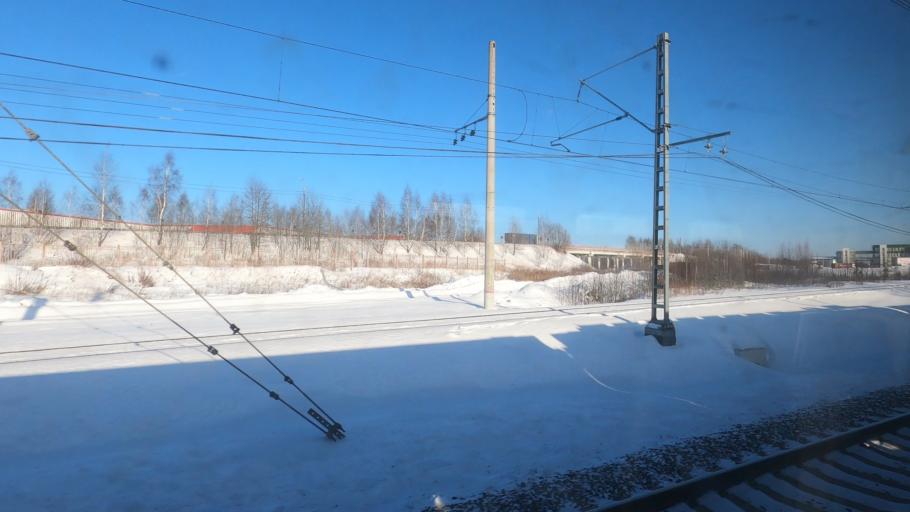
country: RU
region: Moskovskaya
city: Elektrougli
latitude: 55.7250
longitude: 38.2199
